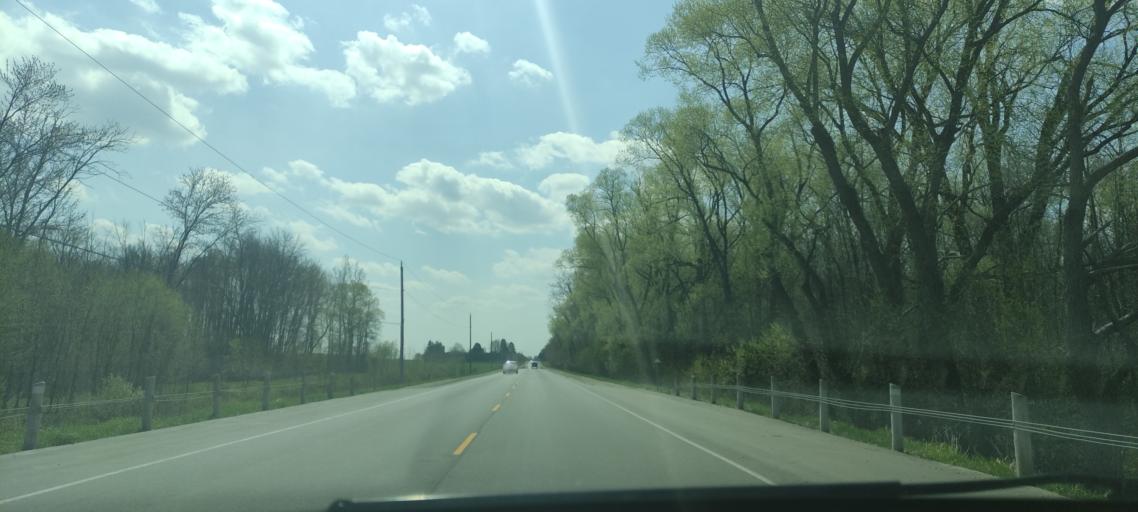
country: CA
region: Ontario
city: Stratford
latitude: 43.3420
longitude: -80.9991
